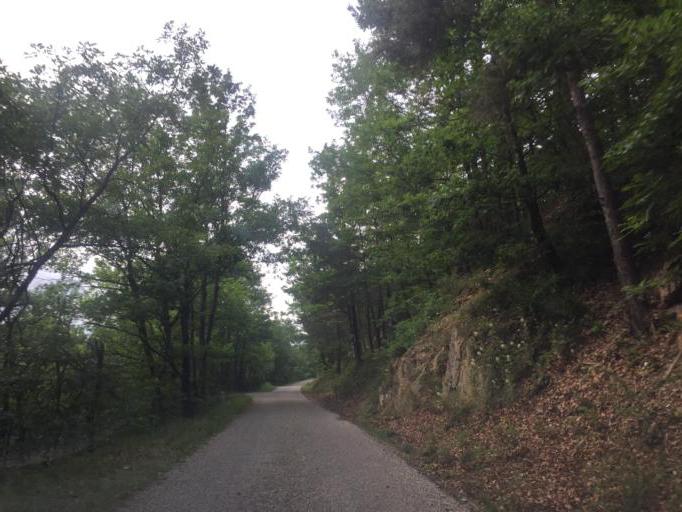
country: FR
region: Rhone-Alpes
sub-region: Departement de l'Ardeche
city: Flaviac
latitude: 44.7885
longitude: 4.6510
